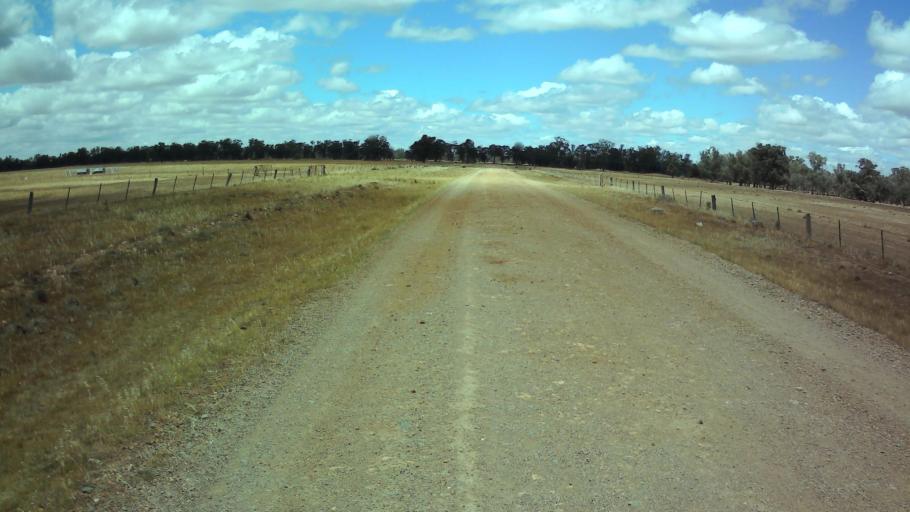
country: AU
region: New South Wales
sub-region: Weddin
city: Grenfell
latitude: -34.0271
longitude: 147.9133
